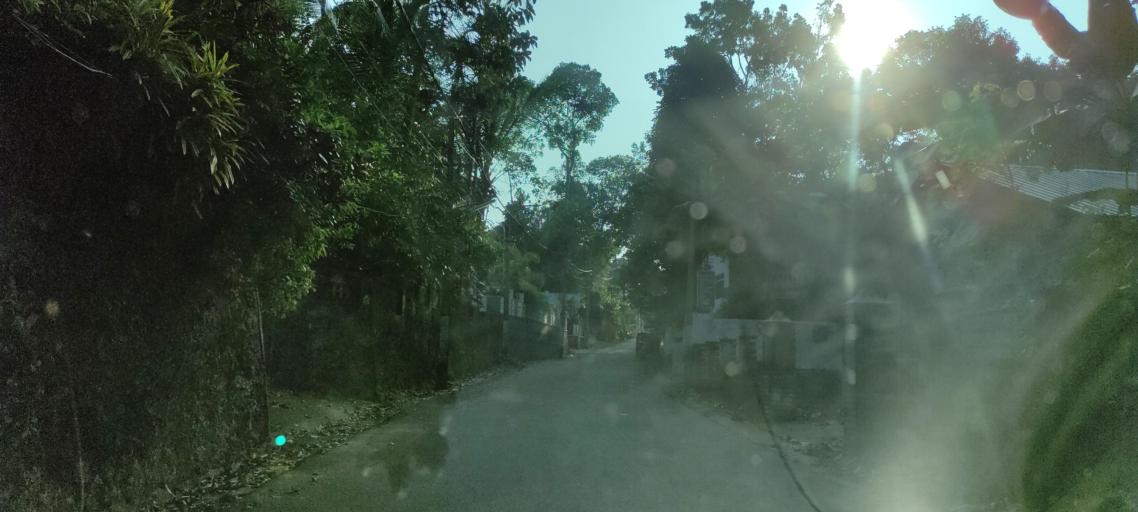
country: IN
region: Kerala
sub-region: Pattanamtitta
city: Adur
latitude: 9.1478
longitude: 76.7483
